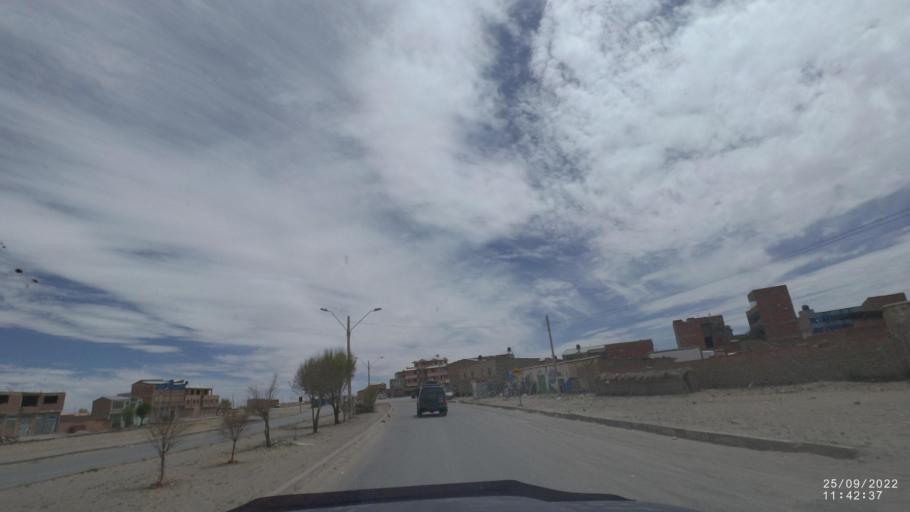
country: BO
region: Oruro
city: Challapata
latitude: -18.8951
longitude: -66.7765
